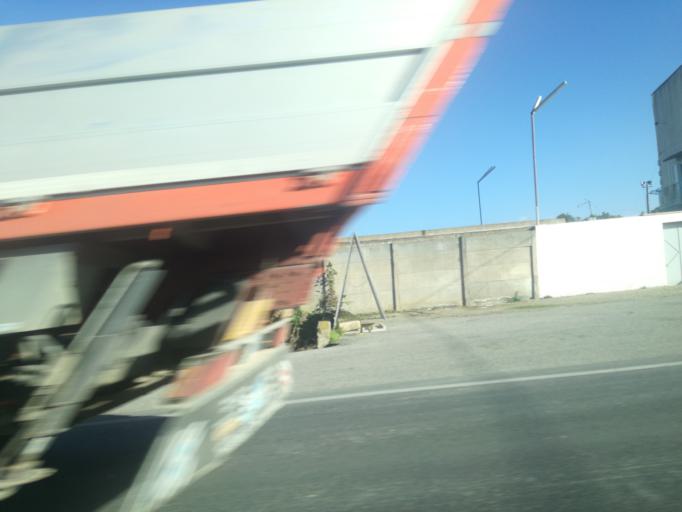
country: IT
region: Sicily
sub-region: Provincia di Caltanissetta
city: Gela
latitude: 37.0573
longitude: 14.2905
